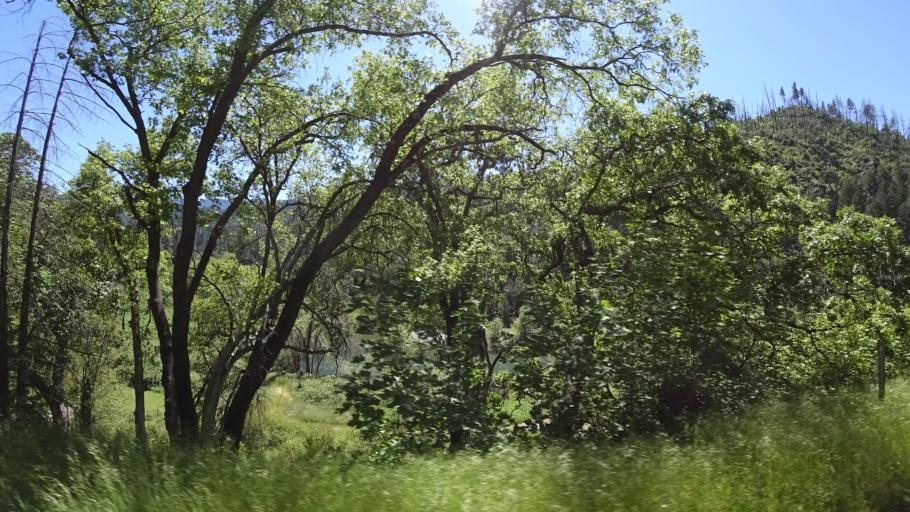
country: US
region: California
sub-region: Trinity County
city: Hayfork
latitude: 40.7474
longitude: -123.2710
